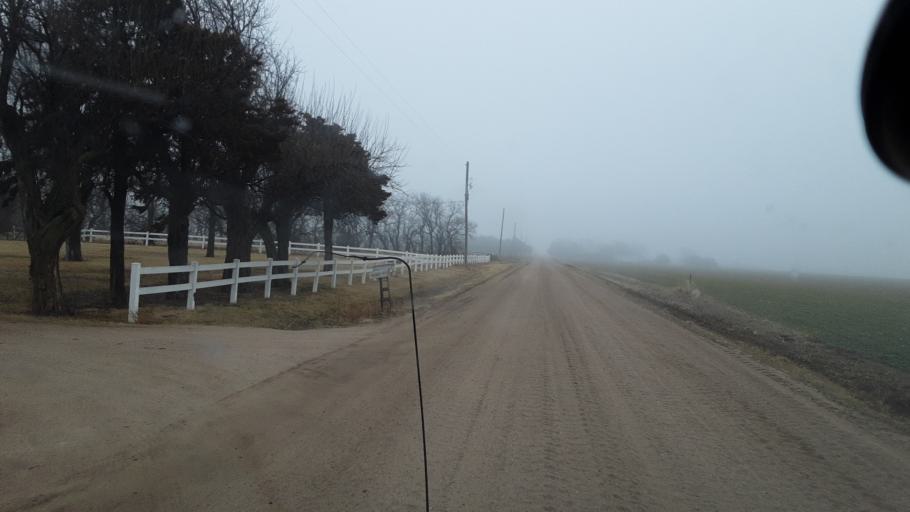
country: US
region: Kansas
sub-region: Reno County
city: South Hutchinson
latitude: 37.9846
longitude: -98.0093
